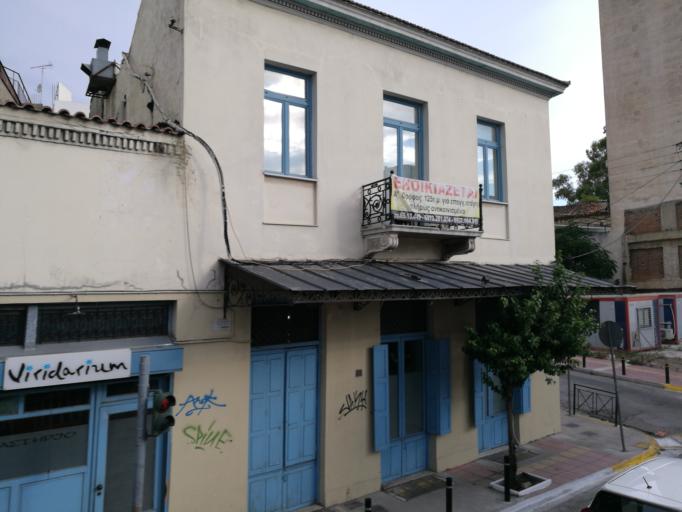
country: GR
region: Attica
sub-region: Nomos Attikis
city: Piraeus
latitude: 37.9484
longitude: 23.6509
